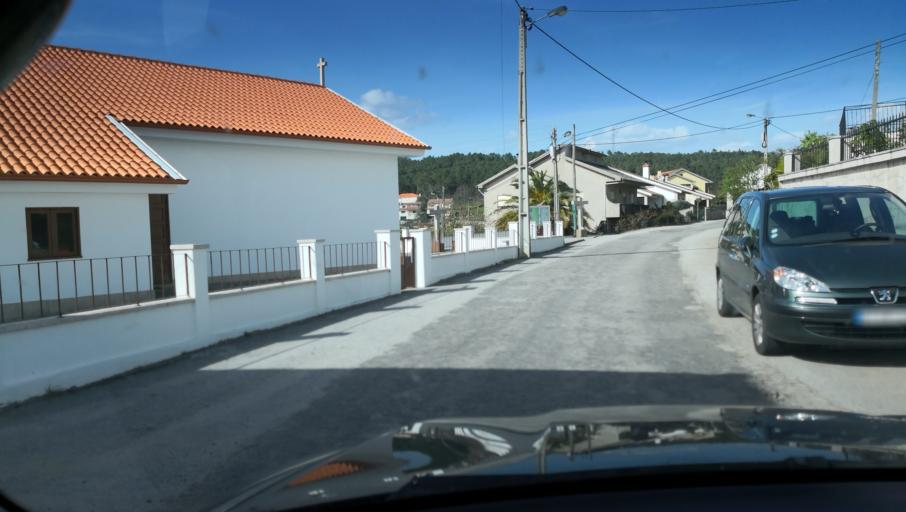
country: PT
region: Vila Real
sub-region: Sabrosa
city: Vilela
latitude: 41.2669
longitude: -7.6599
